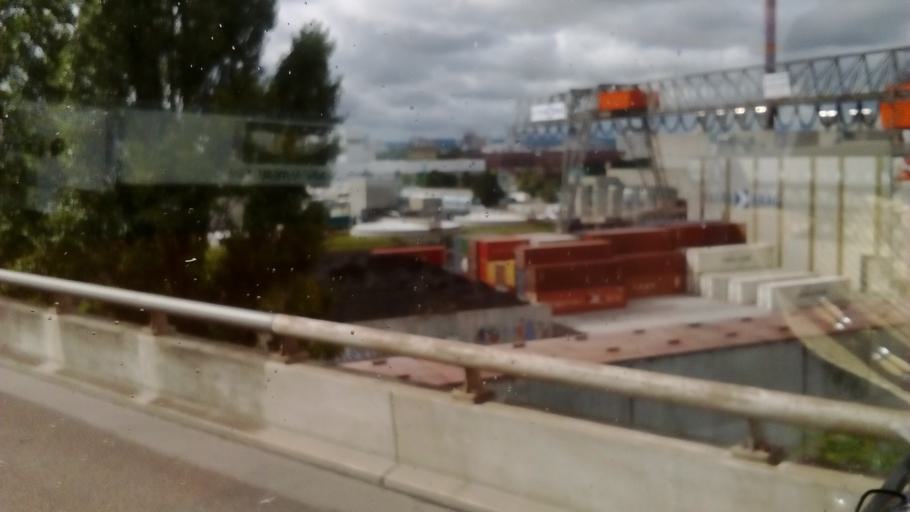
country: DE
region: Baden-Wuerttemberg
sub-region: Freiburg Region
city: Weil am Rhein
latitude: 47.5848
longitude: 7.6019
